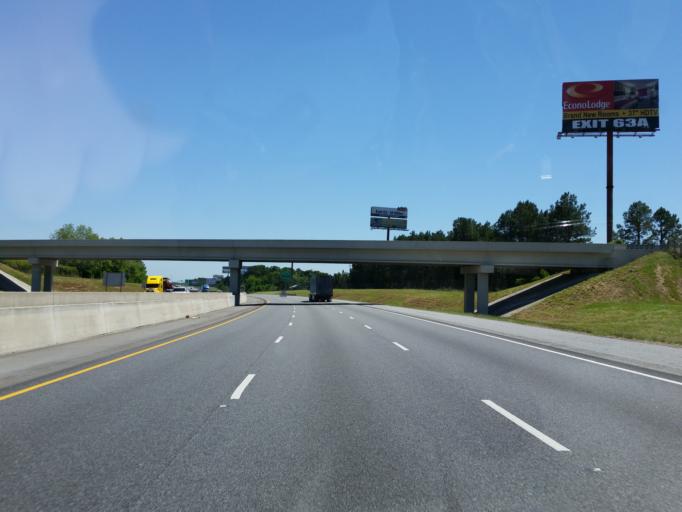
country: US
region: Georgia
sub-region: Turner County
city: Ashburn
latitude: 31.6921
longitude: -83.6286
